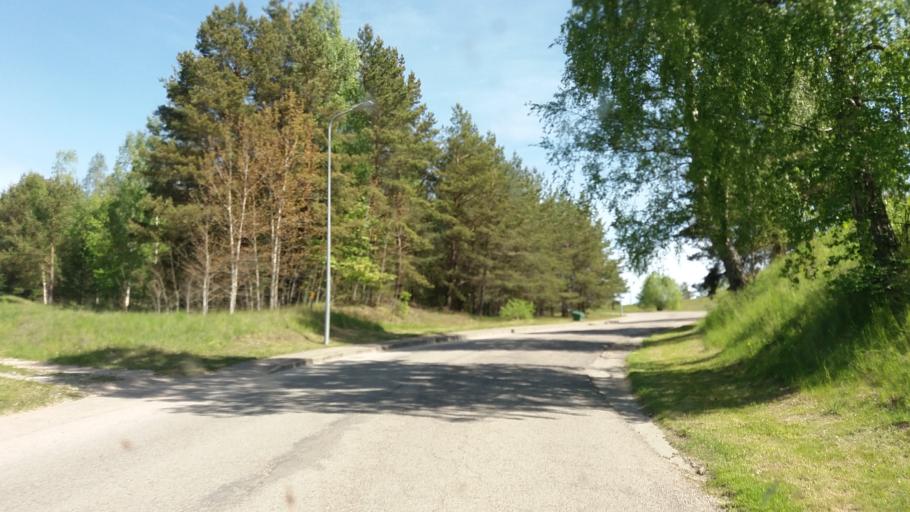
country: LV
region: Talsu Rajons
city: Sabile
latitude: 57.0486
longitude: 22.5762
